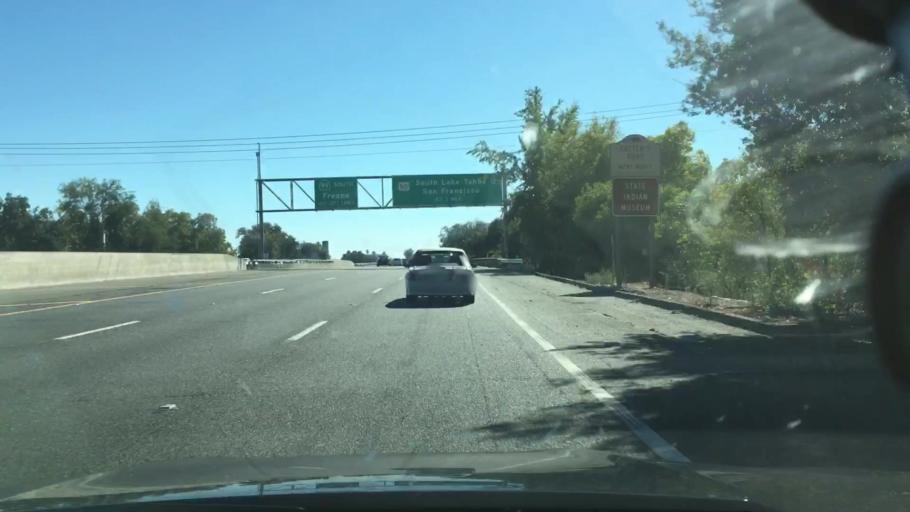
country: US
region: California
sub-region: Sacramento County
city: Sacramento
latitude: 38.5797
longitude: -121.4647
